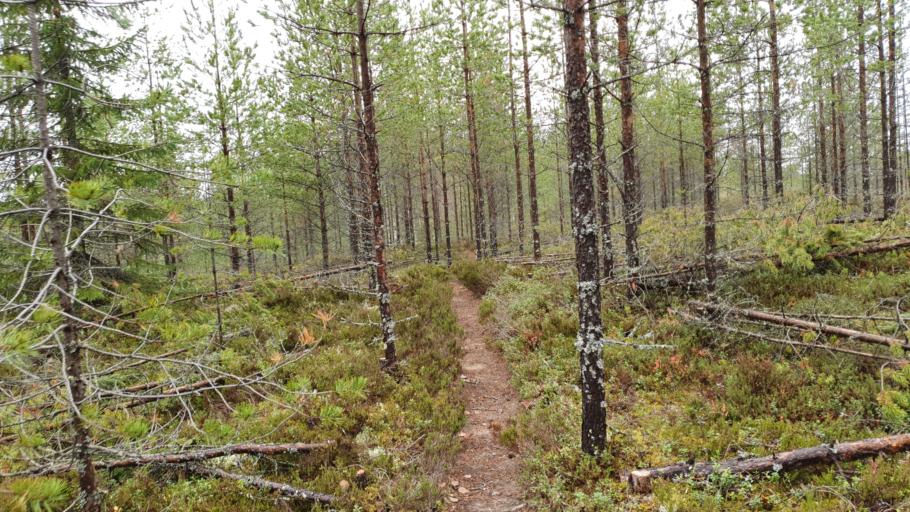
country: FI
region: Kainuu
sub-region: Kehys-Kainuu
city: Kuhmo
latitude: 64.1510
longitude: 29.3976
